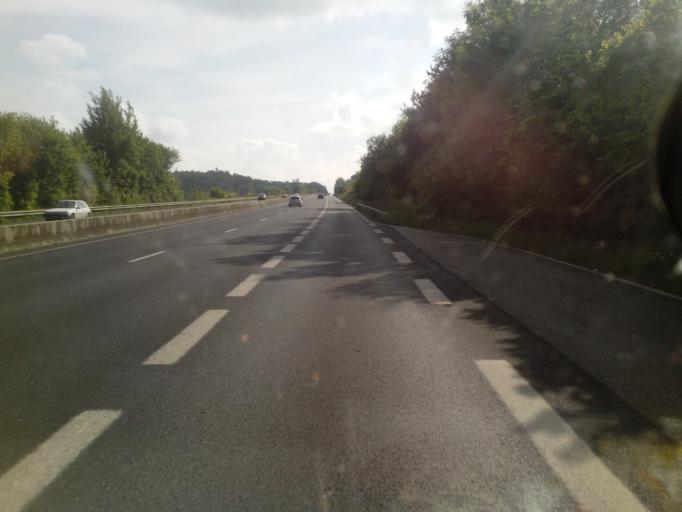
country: FR
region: Haute-Normandie
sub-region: Departement de la Seine-Maritime
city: Mesnieres-en-Bray
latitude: 49.7097
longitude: 1.3800
